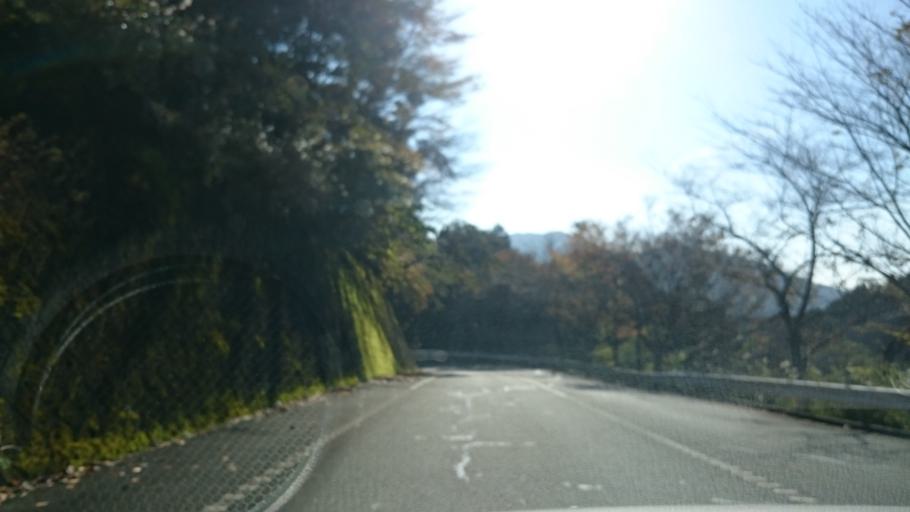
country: JP
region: Shizuoka
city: Heda
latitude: 34.9766
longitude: 138.8156
